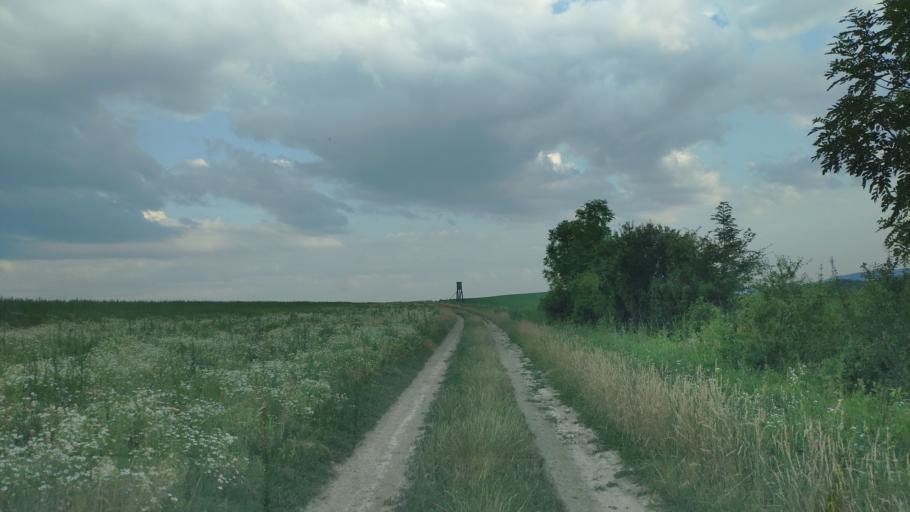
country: SK
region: Kosicky
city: Moldava nad Bodvou
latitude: 48.6938
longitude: 20.9890
